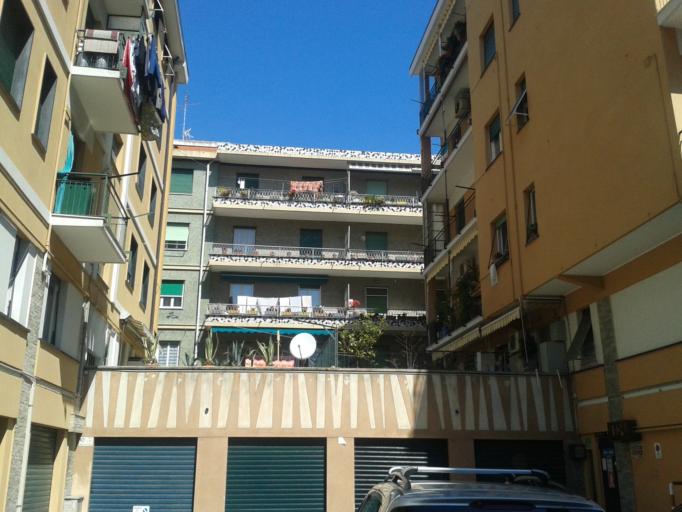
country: IT
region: Liguria
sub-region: Provincia di Savona
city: Albisola Marina
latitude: 44.3318
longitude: 8.5135
